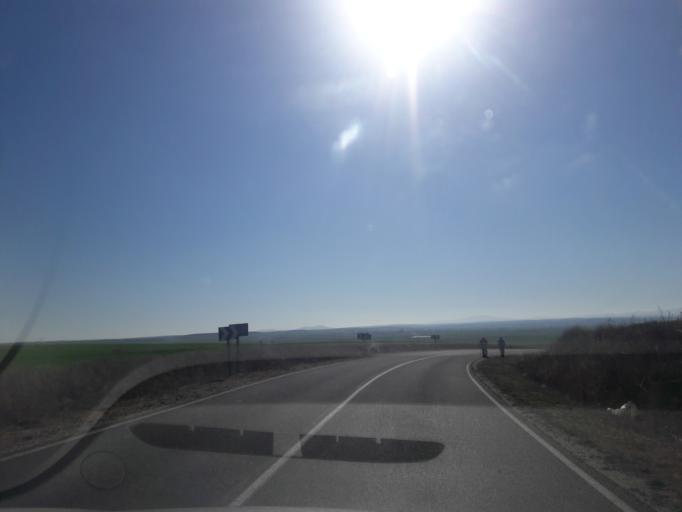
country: ES
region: Castille and Leon
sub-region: Provincia de Salamanca
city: Macotera
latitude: 40.8217
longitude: -5.2661
